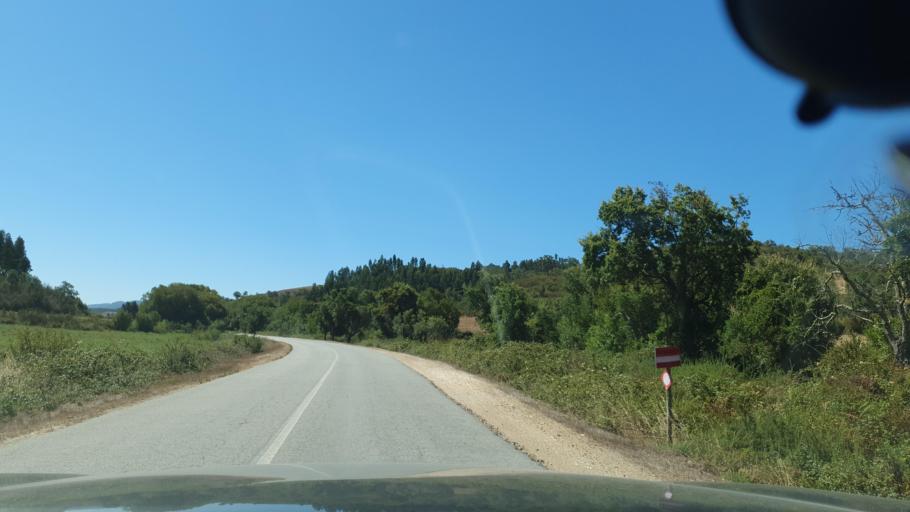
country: PT
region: Beja
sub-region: Odemira
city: Sao Teotonio
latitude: 37.4854
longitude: -8.6345
